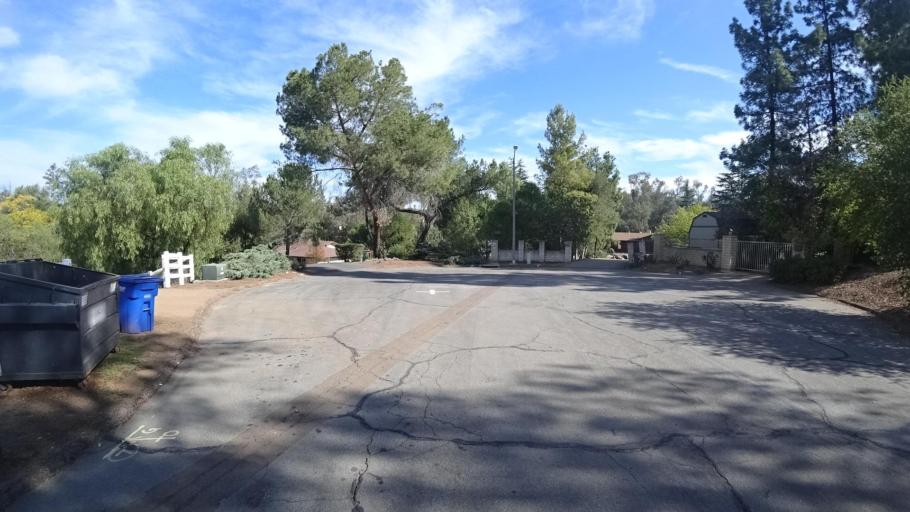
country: US
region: California
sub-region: San Diego County
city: Alpine
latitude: 32.8256
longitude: -116.7820
